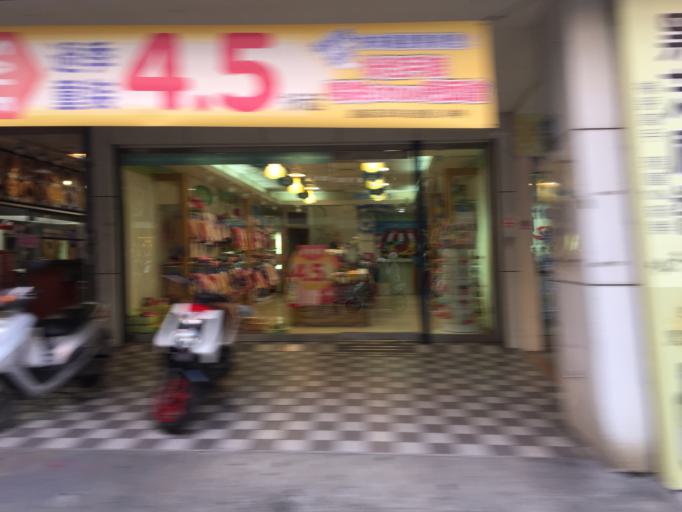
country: TW
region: Taiwan
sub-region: Hsinchu
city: Hsinchu
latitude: 24.8072
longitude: 120.9615
